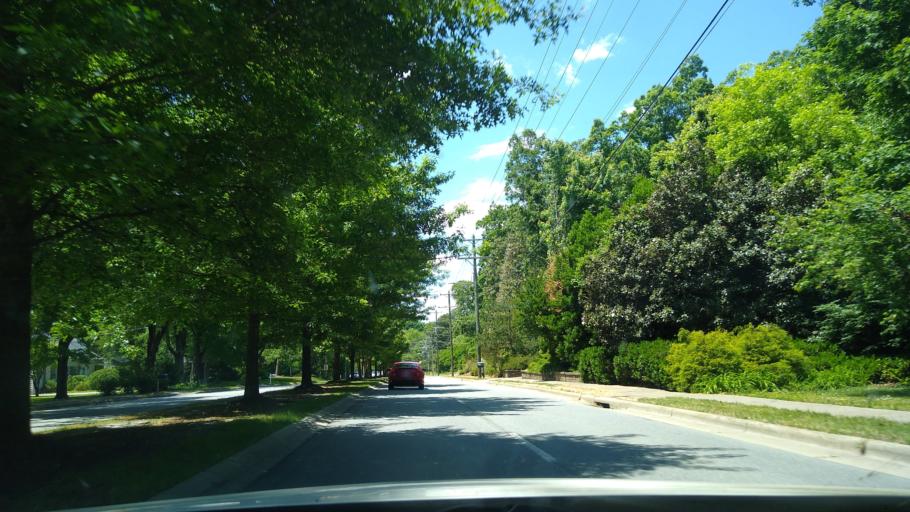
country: US
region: North Carolina
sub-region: Guilford County
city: Greensboro
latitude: 36.0910
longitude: -79.8610
